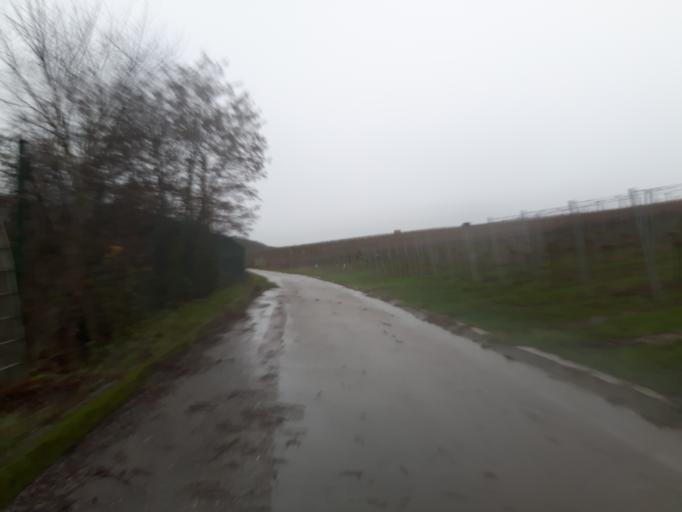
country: DE
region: Baden-Wuerttemberg
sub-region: Regierungsbezirk Stuttgart
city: Erlenbach
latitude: 49.1637
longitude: 9.2489
